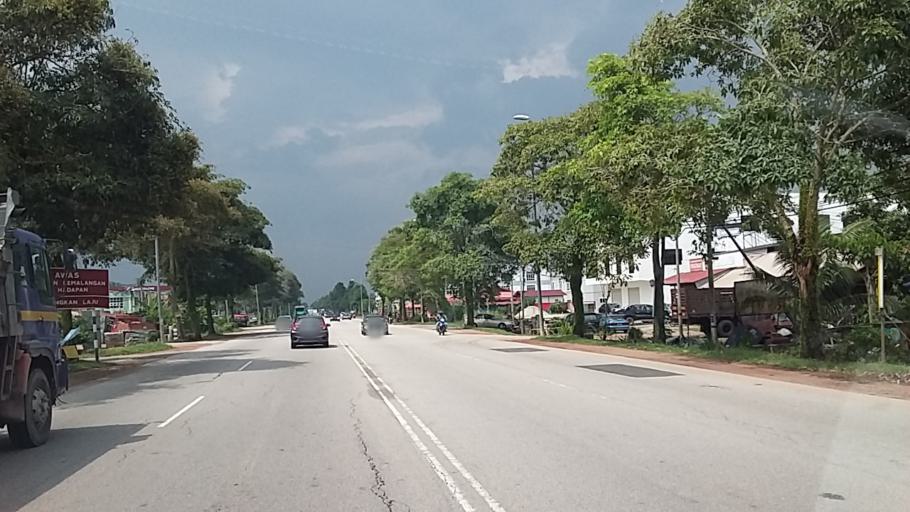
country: MY
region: Johor
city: Parit Raja
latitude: 1.8671
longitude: 103.1178
